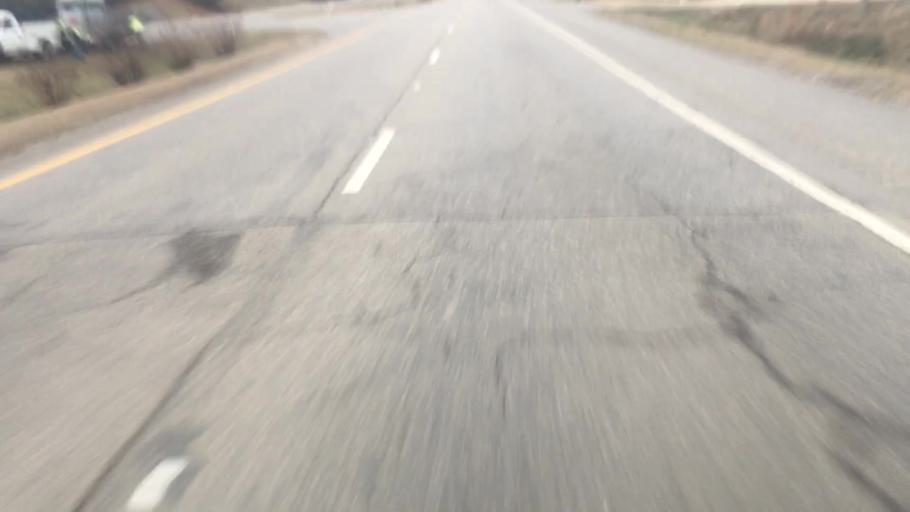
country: US
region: Alabama
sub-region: Walker County
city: Sumiton
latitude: 33.7403
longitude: -87.0341
